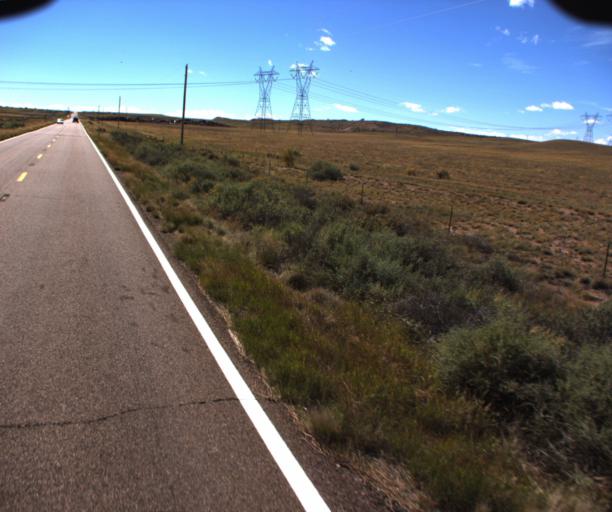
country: US
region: Arizona
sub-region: Apache County
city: Saint Johns
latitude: 34.5798
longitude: -109.3336
